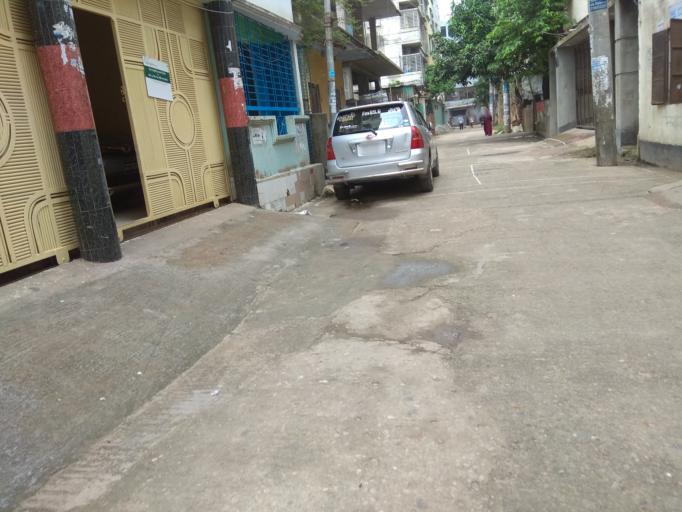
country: BD
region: Dhaka
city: Azimpur
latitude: 23.8036
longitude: 90.3546
